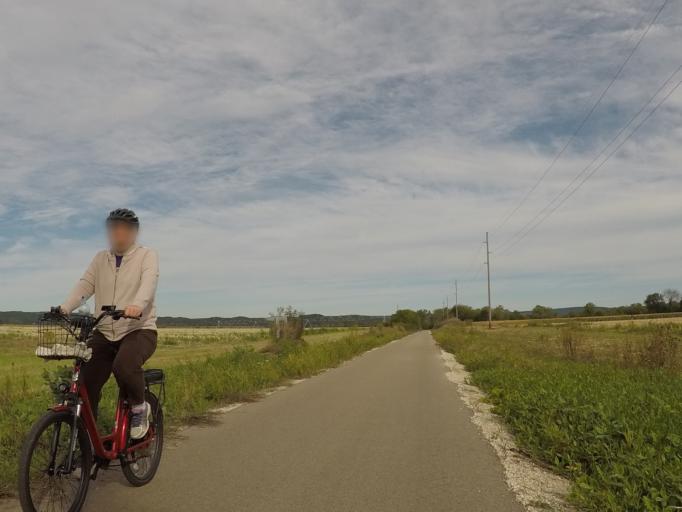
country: US
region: Wisconsin
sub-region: Sauk County
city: Prairie du Sac
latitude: 43.3224
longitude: -89.7431
